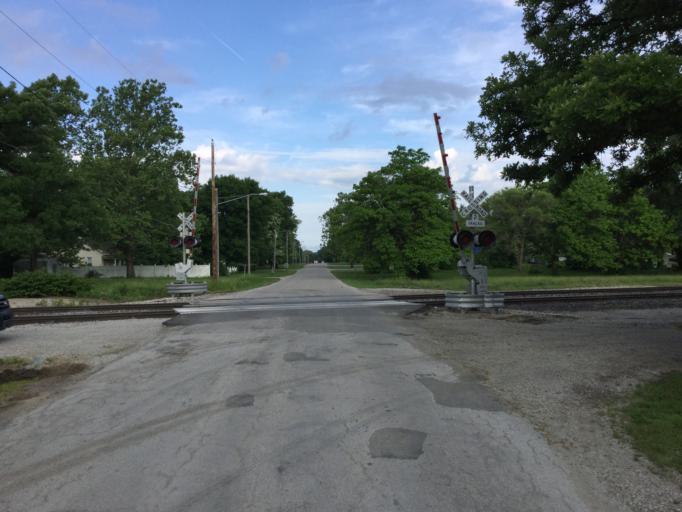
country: US
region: Kansas
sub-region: Linn County
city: Pleasanton
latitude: 38.1716
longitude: -94.7070
